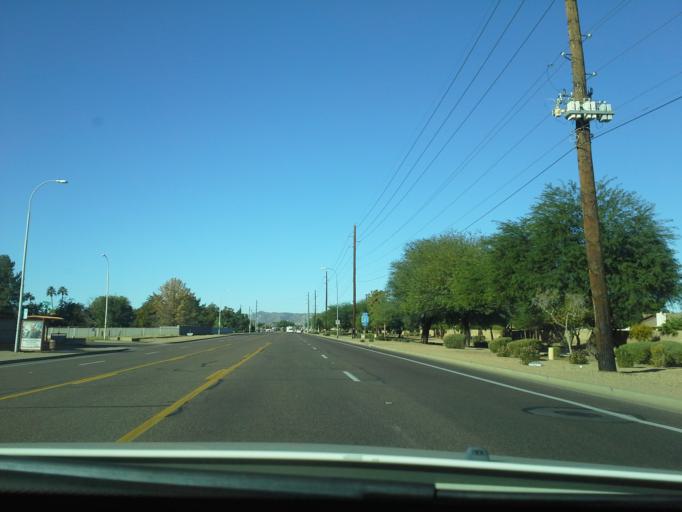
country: US
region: Arizona
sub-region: Maricopa County
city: San Carlos
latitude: 33.3495
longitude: -111.8869
